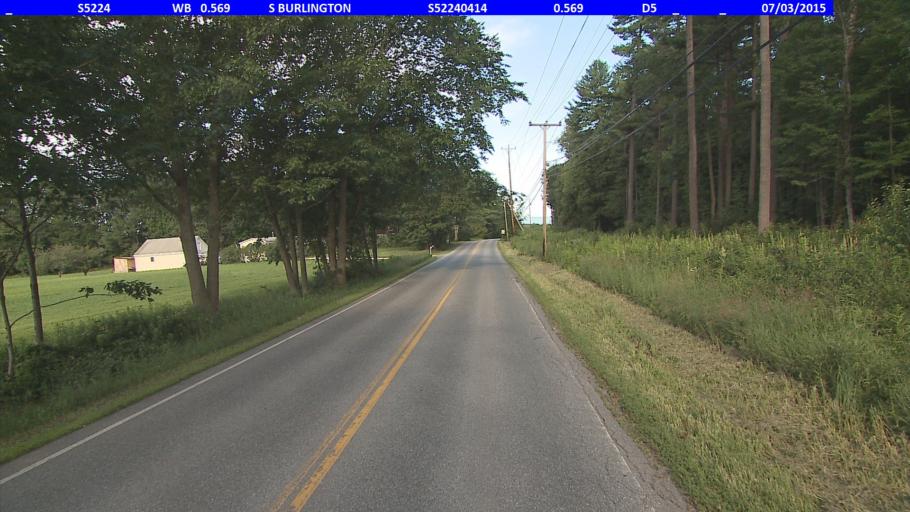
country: US
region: Vermont
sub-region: Chittenden County
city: Burlington
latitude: 44.4453
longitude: -73.1978
